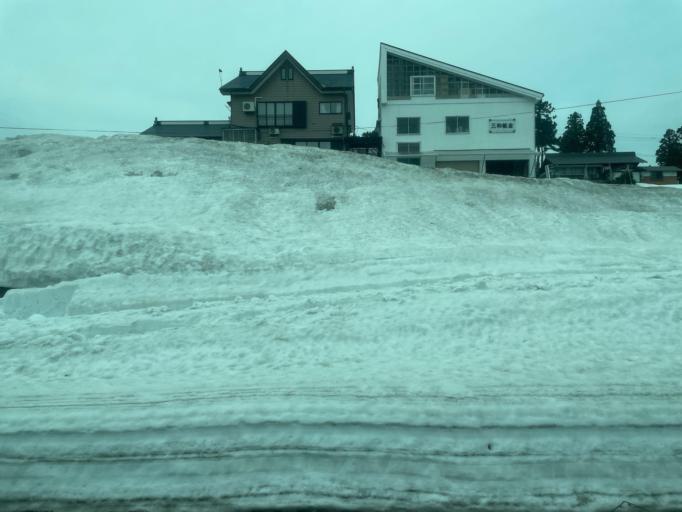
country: JP
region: Niigata
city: Shiozawa
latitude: 37.0329
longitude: 138.8347
